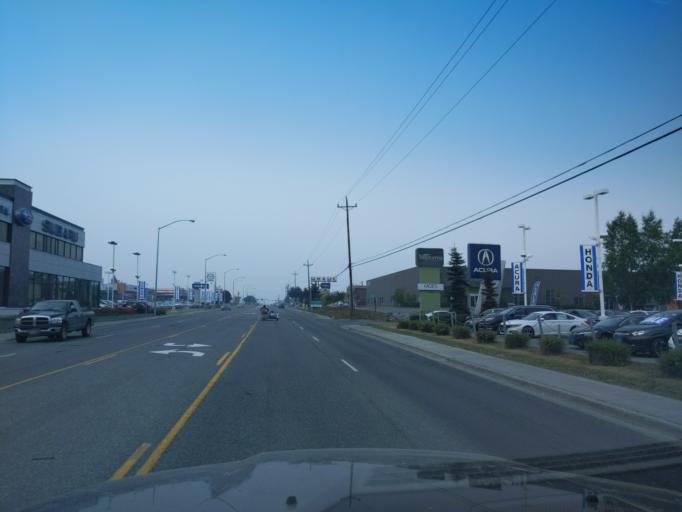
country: US
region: Alaska
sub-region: Anchorage Municipality
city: Anchorage
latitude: 61.1753
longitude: -149.8681
